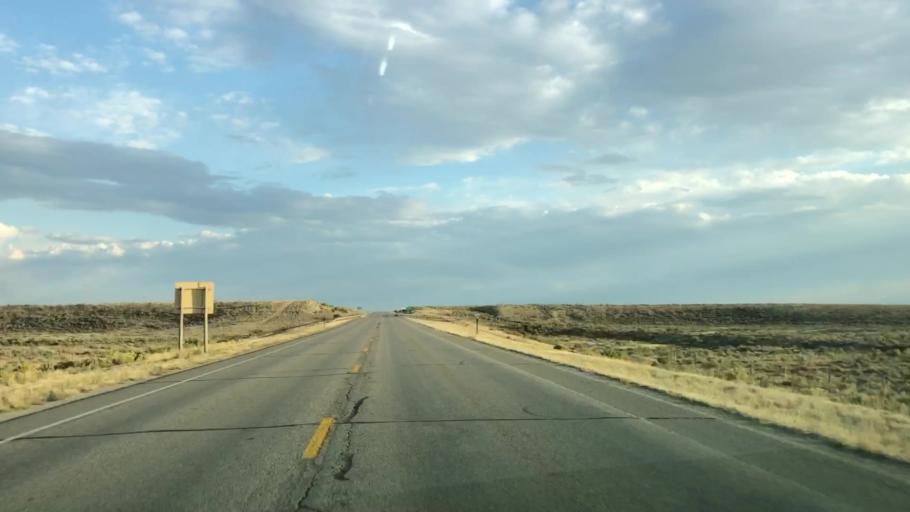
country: US
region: Wyoming
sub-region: Sweetwater County
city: North Rock Springs
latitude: 42.1019
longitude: -109.4465
